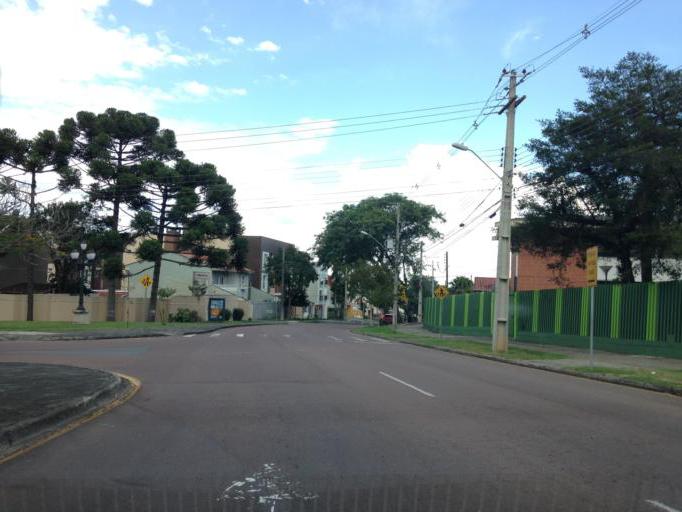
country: BR
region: Parana
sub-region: Curitiba
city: Curitiba
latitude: -25.4124
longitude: -49.2320
